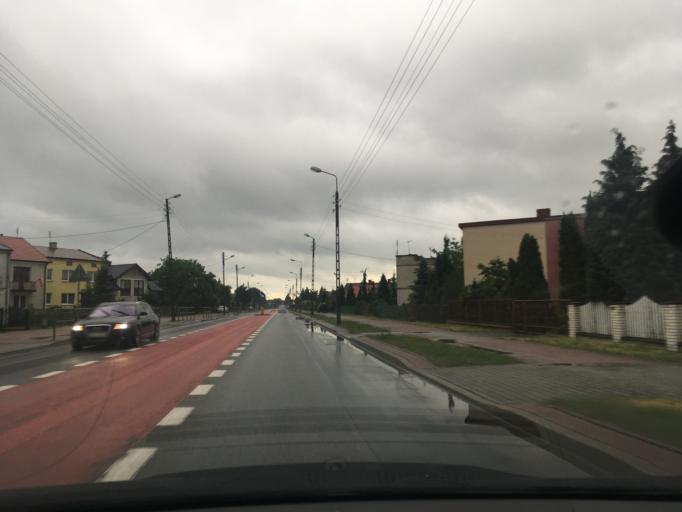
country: PL
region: Lublin Voivodeship
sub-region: Powiat rycki
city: Deblin
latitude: 51.5673
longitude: 21.8804
